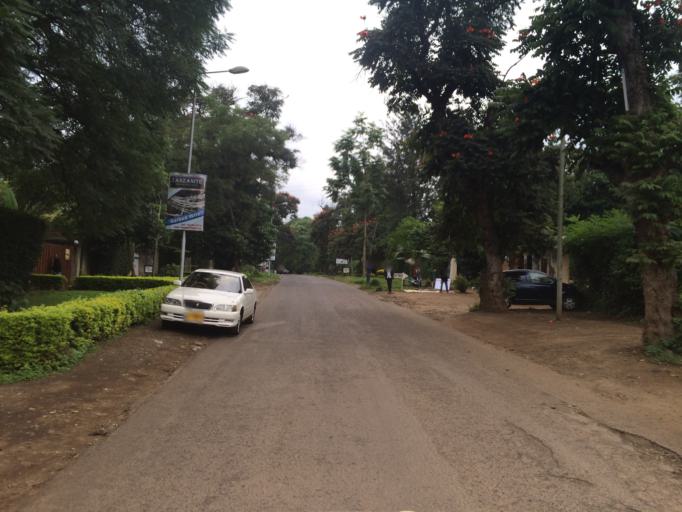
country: TZ
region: Arusha
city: Arusha
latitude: -3.3750
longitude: 36.7008
